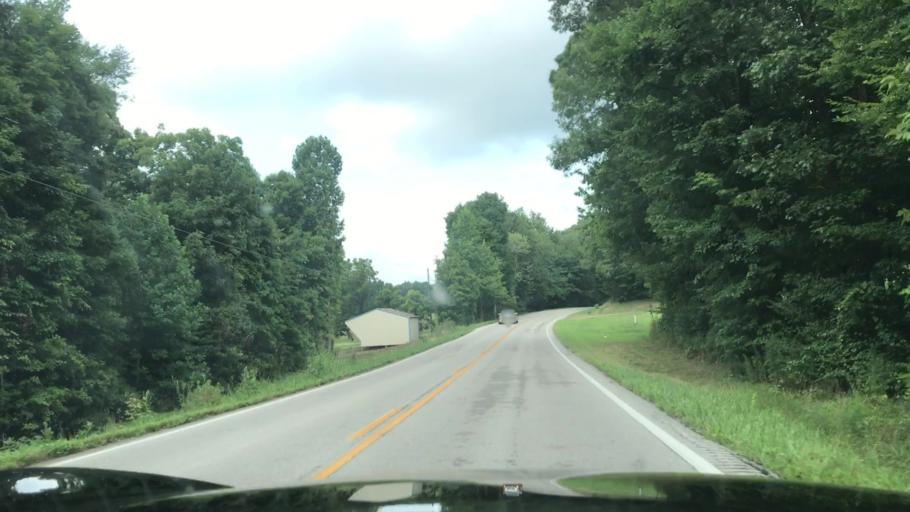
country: US
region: Kentucky
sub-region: Butler County
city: Morgantown
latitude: 37.1726
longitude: -86.8337
